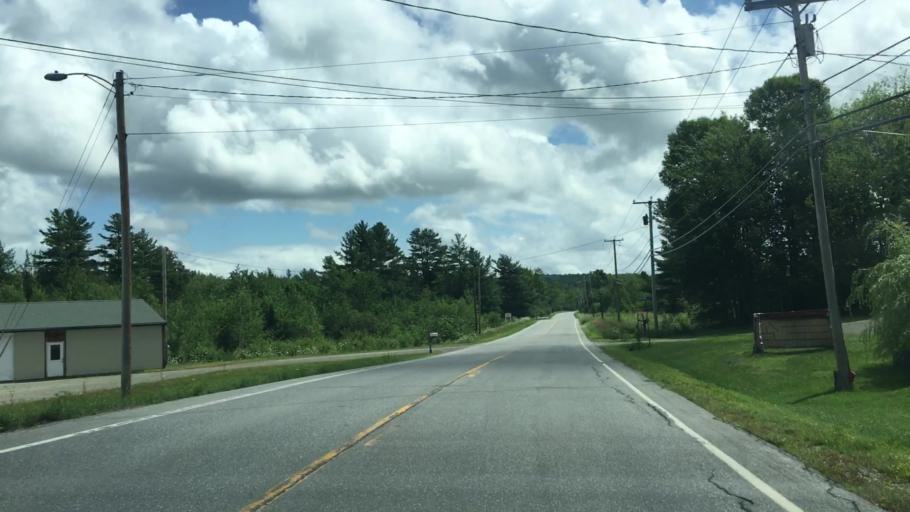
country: US
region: Maine
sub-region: Penobscot County
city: Hermon
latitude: 44.8090
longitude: -68.9779
